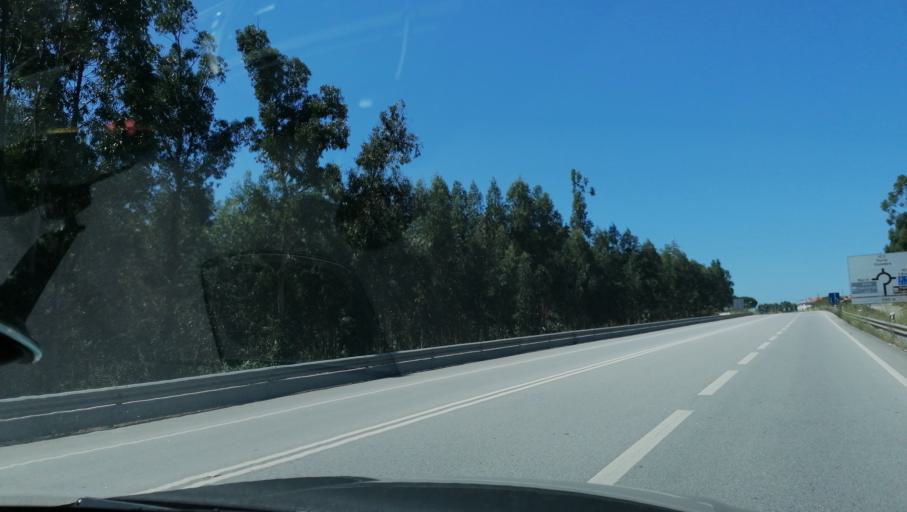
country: PT
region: Aveiro
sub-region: Agueda
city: Agueda
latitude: 40.5576
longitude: -8.4602
